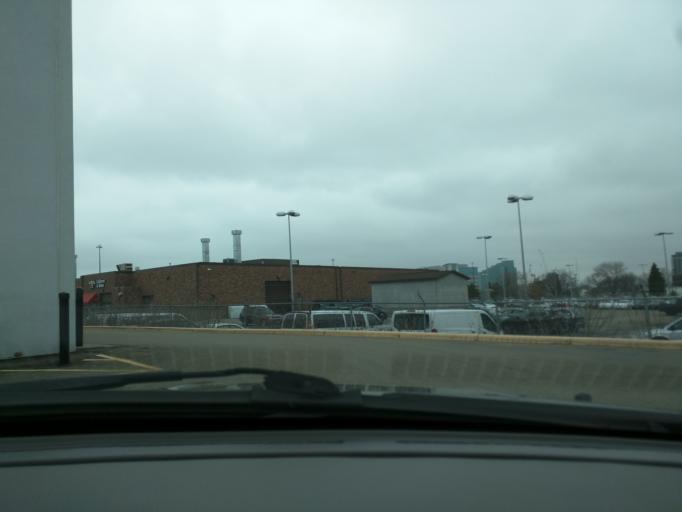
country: US
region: Minnesota
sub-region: Hennepin County
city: Edina
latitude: 44.8564
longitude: -93.3431
